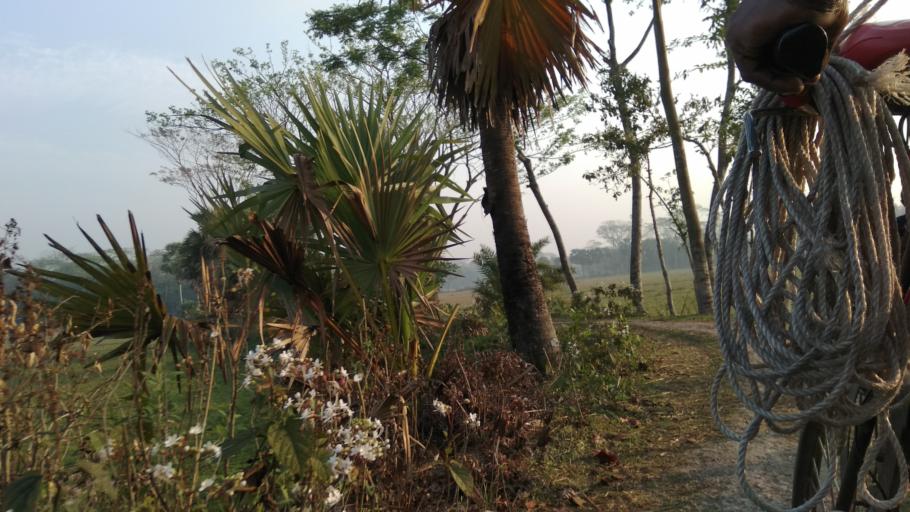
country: BD
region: Barisal
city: Mehendiganj
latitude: 22.9345
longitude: 90.4136
